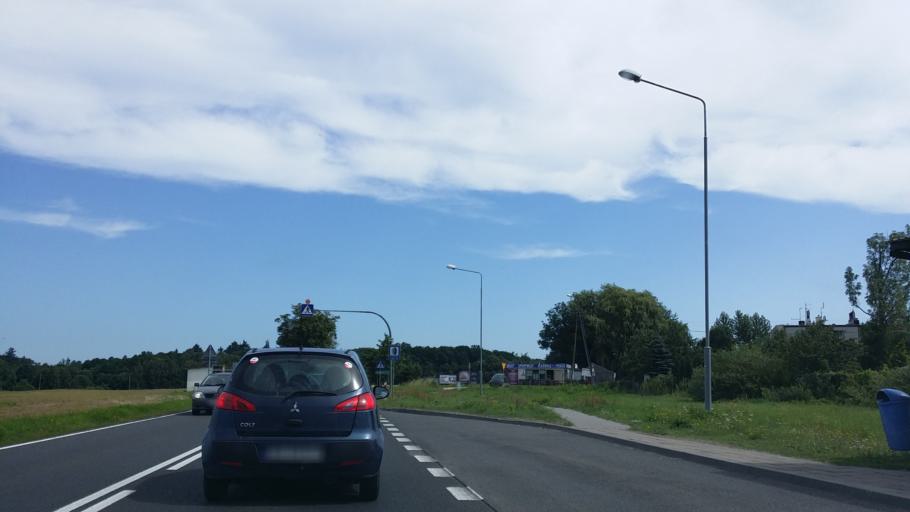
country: PL
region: West Pomeranian Voivodeship
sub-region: Powiat kolobrzeski
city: Kolobrzeg
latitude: 54.1811
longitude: 15.6326
